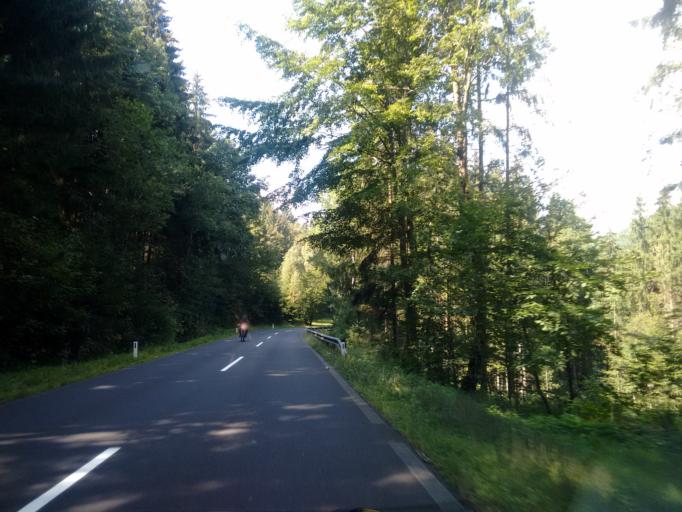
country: AT
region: Upper Austria
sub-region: Politischer Bezirk Urfahr-Umgebung
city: Altenberg bei Linz
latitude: 48.3918
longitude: 14.3419
